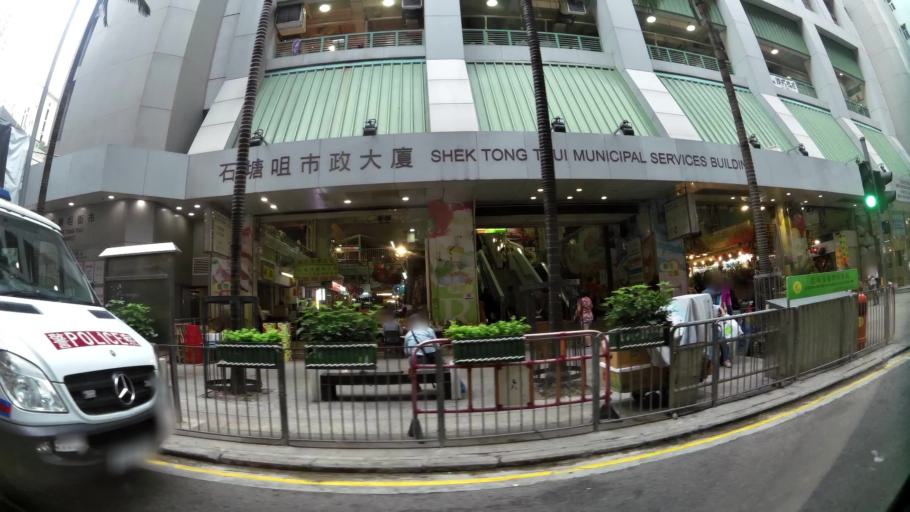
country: HK
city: Hong Kong
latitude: 22.2859
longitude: 114.1370
